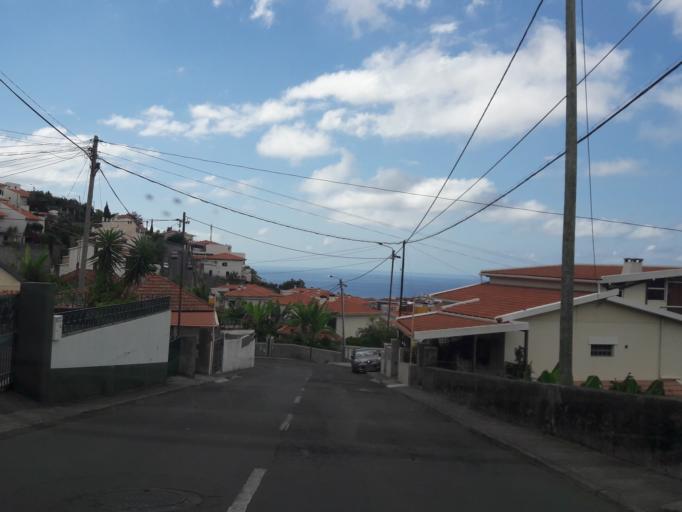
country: PT
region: Madeira
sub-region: Funchal
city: Nossa Senhora do Monte
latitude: 32.6667
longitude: -16.9274
